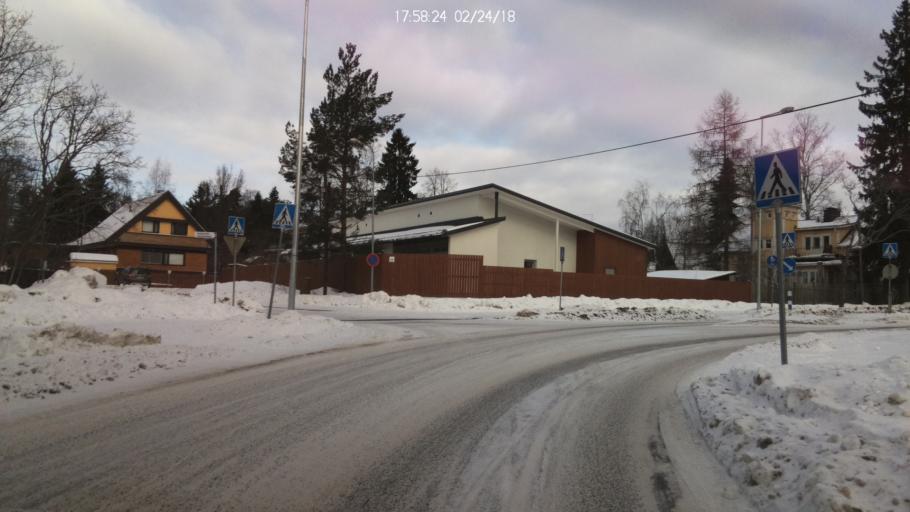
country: FI
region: Uusimaa
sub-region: Helsinki
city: Kilo
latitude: 60.2685
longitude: 24.8141
